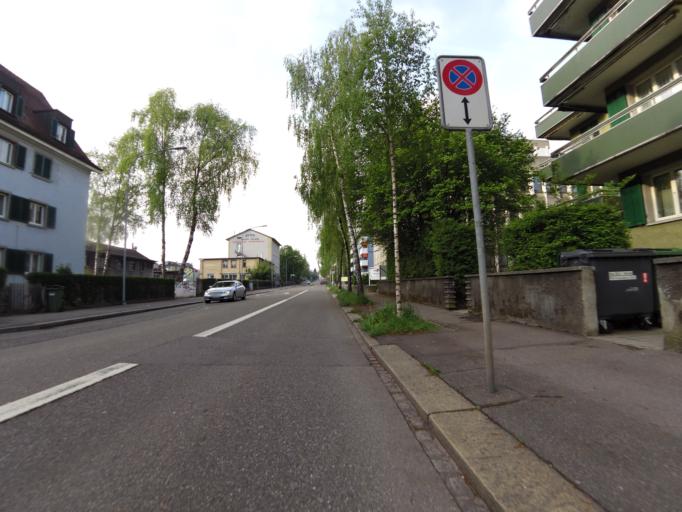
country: CH
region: Zurich
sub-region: Bezirk Zuerich
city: Zuerich (Kreis 11) / Oerlikon
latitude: 47.4092
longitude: 8.5375
